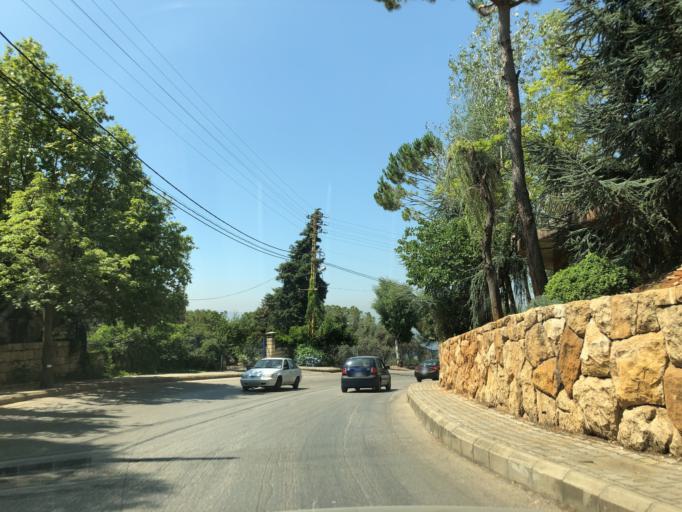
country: LB
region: Mont-Liban
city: Jdaidet el Matn
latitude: 33.8770
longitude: 35.6245
